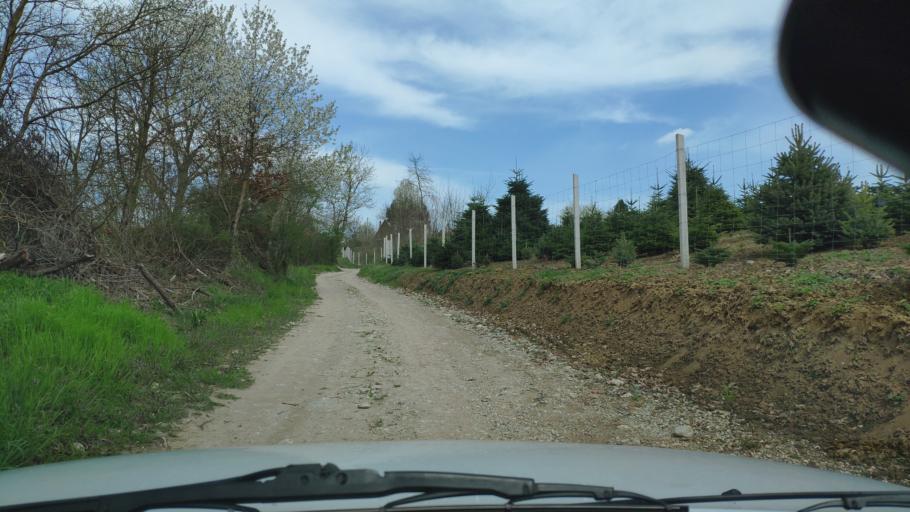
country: HU
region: Zala
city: Nagykanizsa
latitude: 46.4244
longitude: 17.0153
